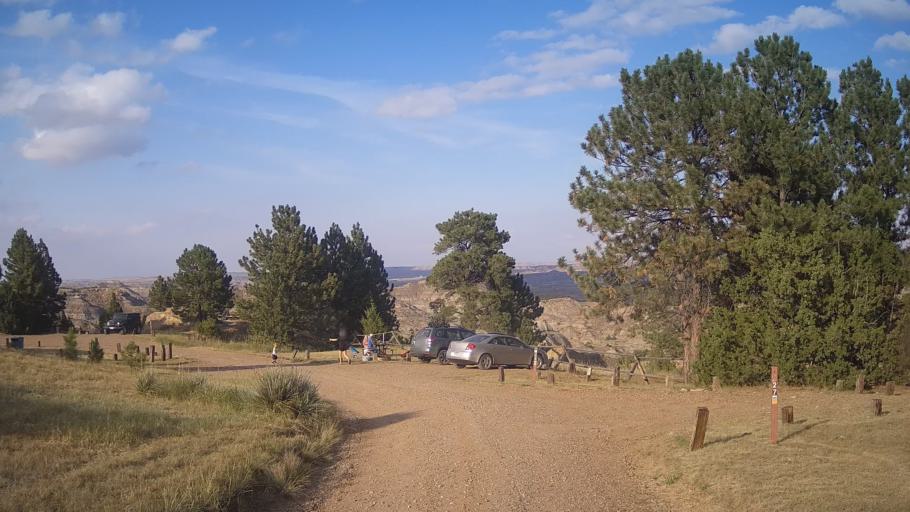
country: US
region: Montana
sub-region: Dawson County
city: Glendive
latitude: 47.0580
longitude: -104.6642
